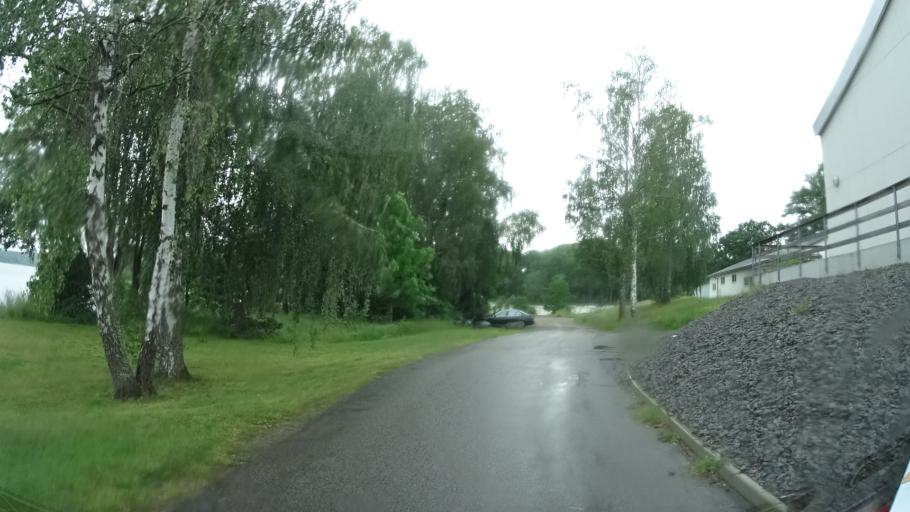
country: SE
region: Kalmar
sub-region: Vasterviks Kommun
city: Gamleby
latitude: 57.8894
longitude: 16.4189
